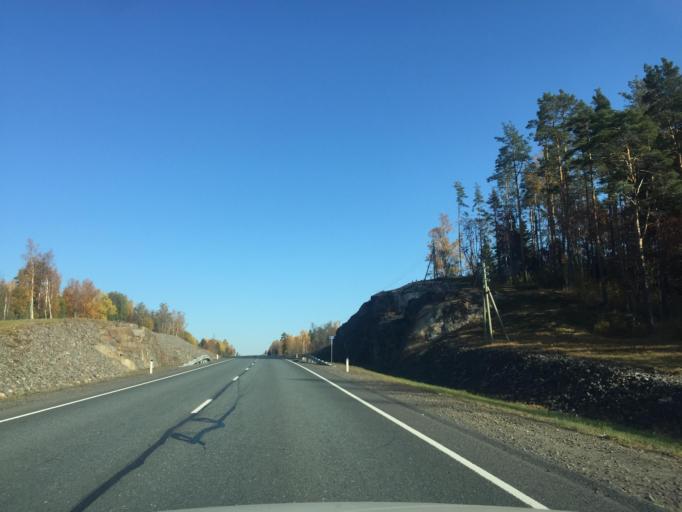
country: RU
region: Leningrad
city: Kuznechnoye
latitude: 61.3498
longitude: 29.8807
